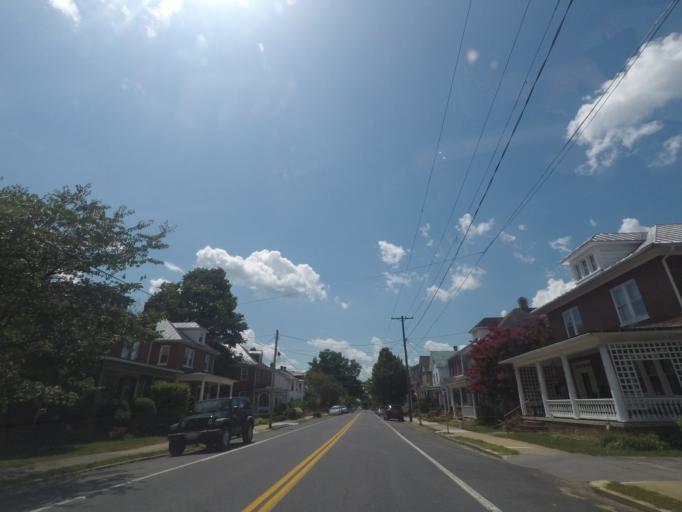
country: US
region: Virginia
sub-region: City of Winchester
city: Winchester
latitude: 39.1919
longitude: -78.1642
